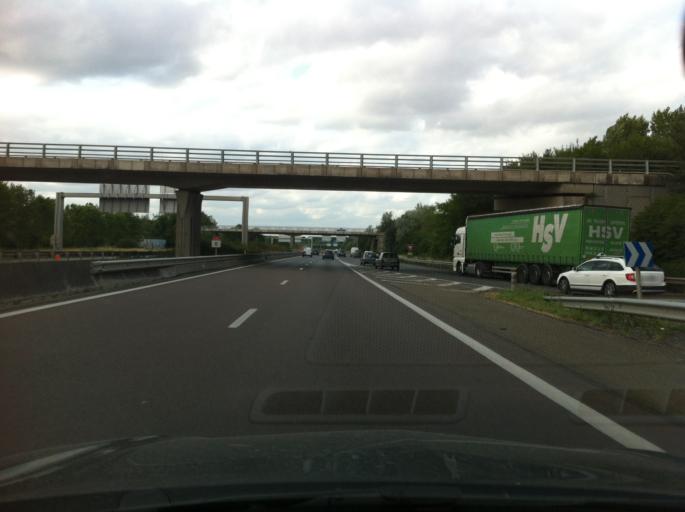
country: FR
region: Ile-de-France
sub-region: Departement de Seine-et-Marne
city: Lieusaint
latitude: 48.6340
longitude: 2.5356
